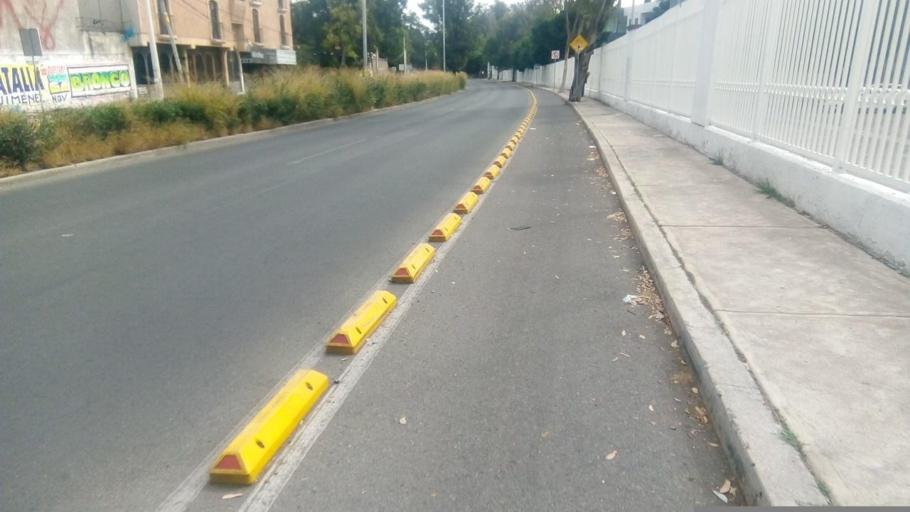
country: MX
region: Queretaro
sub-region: Queretaro
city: Santiago de Queretaro
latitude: 20.6146
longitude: -100.4025
